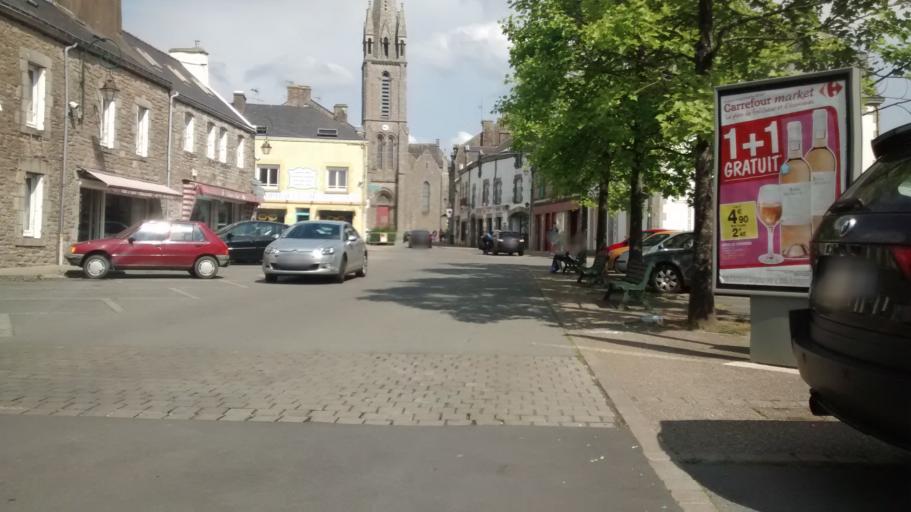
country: FR
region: Brittany
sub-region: Departement du Morbihan
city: Questembert
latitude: 47.6615
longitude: -2.4568
